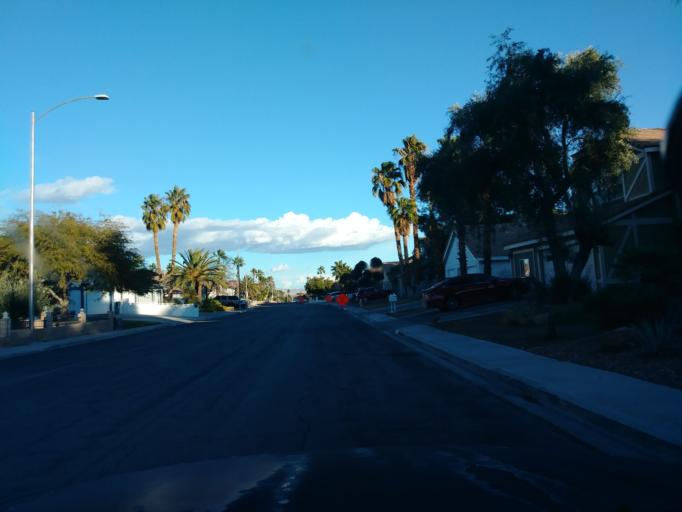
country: US
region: Nevada
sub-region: Clark County
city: Spring Valley
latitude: 36.1464
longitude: -115.2360
